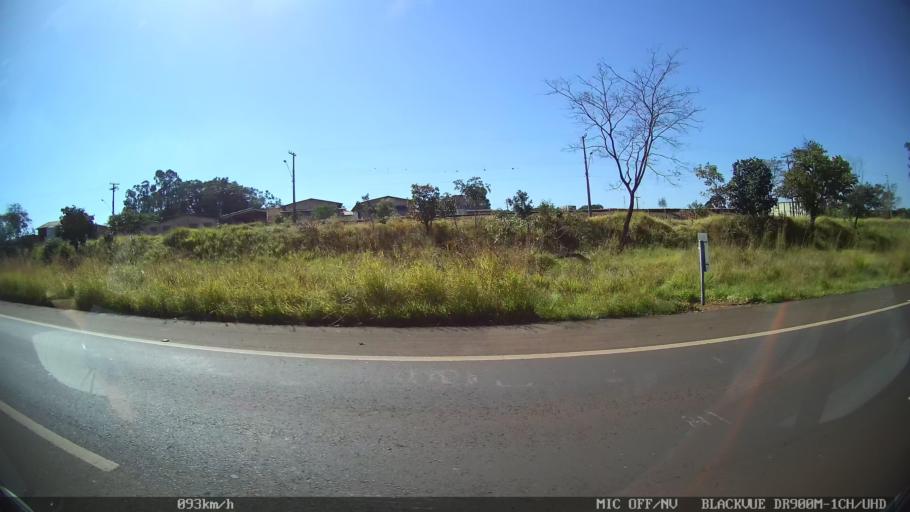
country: BR
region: Sao Paulo
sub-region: Franca
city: Franca
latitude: -20.5548
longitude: -47.4490
